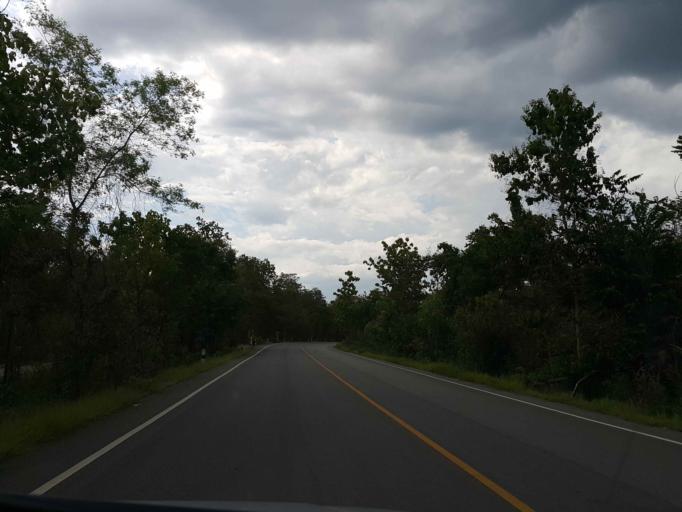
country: TH
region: Sukhothai
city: Thung Saliam
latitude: 17.3773
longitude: 99.4015
